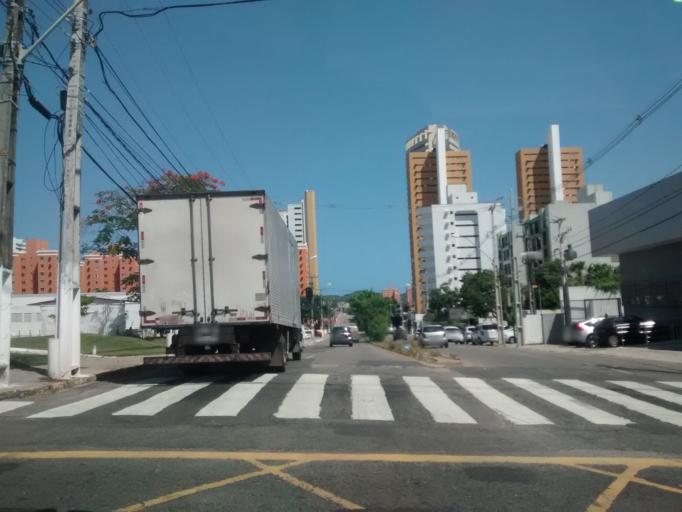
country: BR
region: Rio Grande do Norte
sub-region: Natal
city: Natal
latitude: -5.8191
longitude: -35.2127
